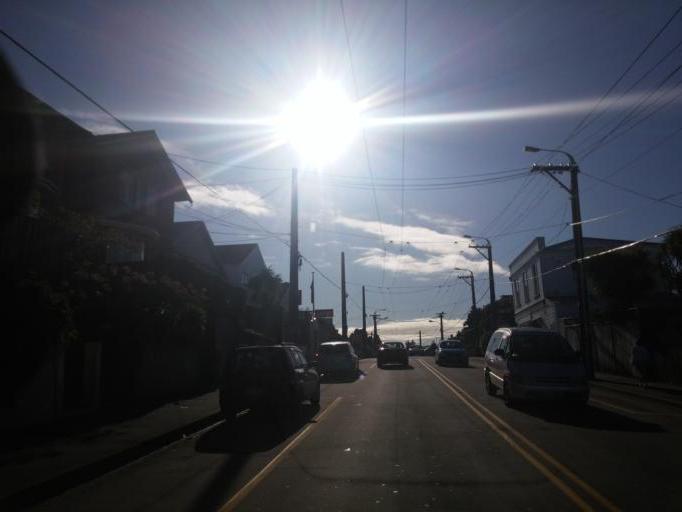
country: NZ
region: Wellington
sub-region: Wellington City
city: Wellington
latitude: -41.3055
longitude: 174.7750
